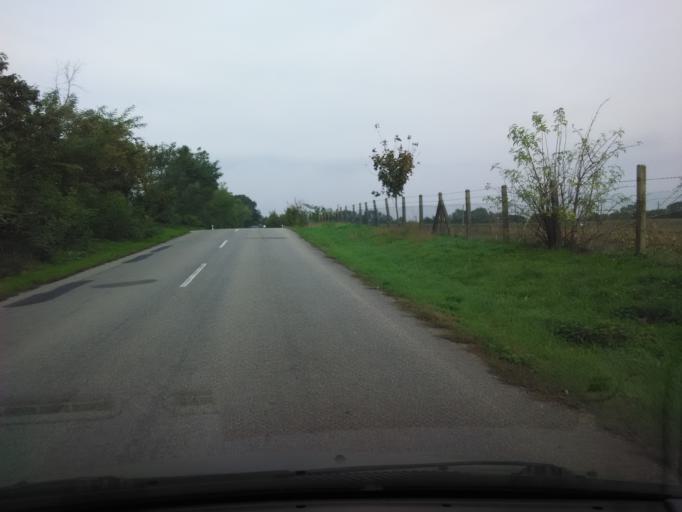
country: SK
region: Nitriansky
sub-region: Okres Nove Zamky
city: Nove Zamky
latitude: 47.9620
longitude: 18.2521
